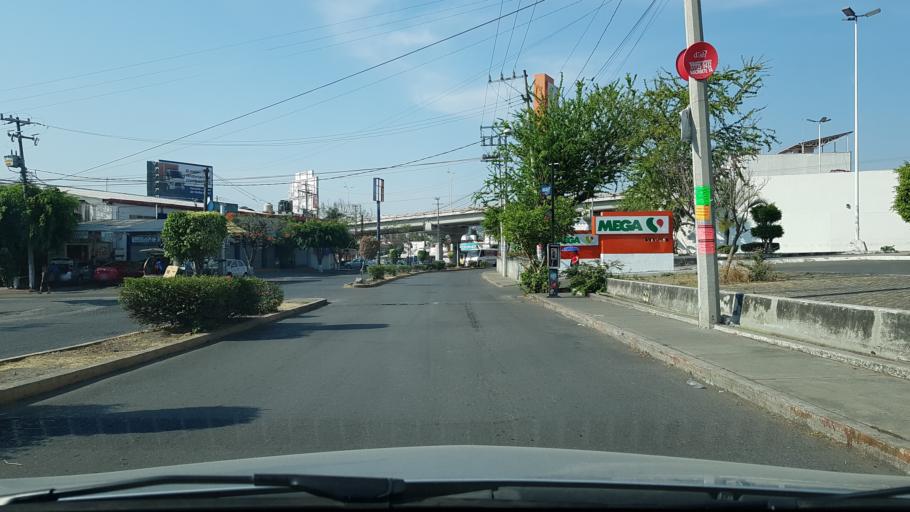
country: MX
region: Morelos
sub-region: Jiutepec
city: Jiutepec
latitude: 18.8965
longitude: -99.1666
